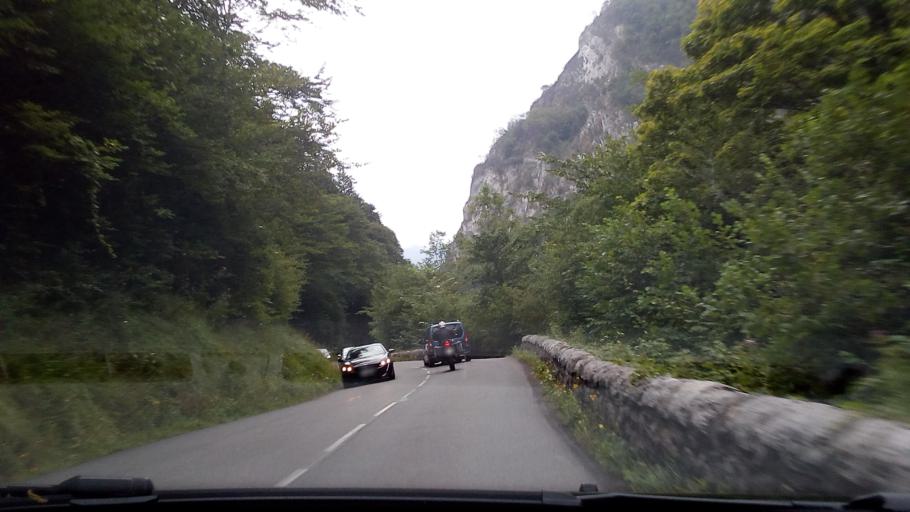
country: FR
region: Aquitaine
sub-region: Departement des Pyrenees-Atlantiques
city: Laruns
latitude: 42.9638
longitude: -0.4402
